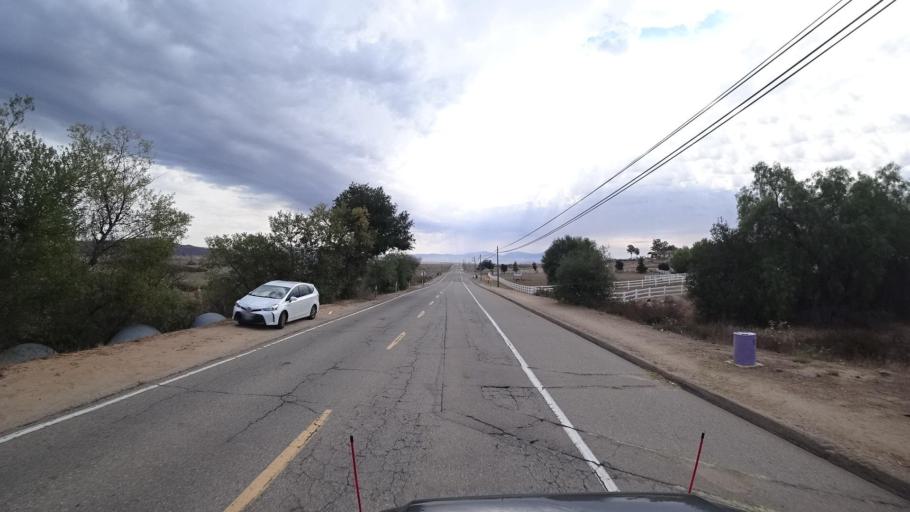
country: US
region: California
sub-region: San Diego County
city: San Pasqual
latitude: 33.0331
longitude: -116.9502
